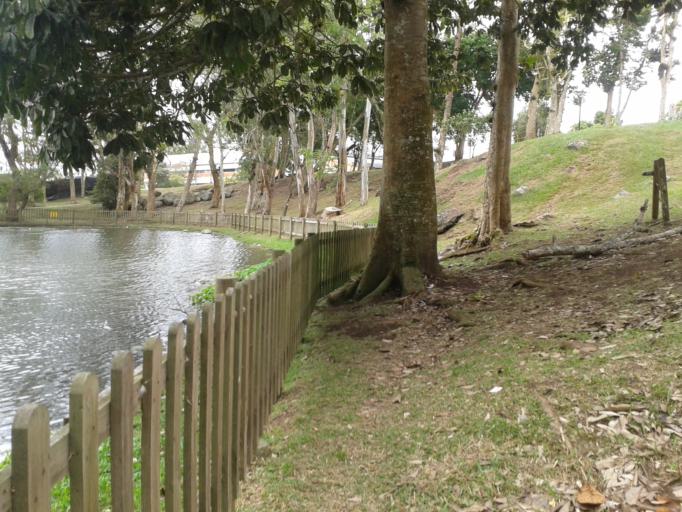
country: CR
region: Cartago
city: Cartago
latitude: 9.8555
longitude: -83.9110
